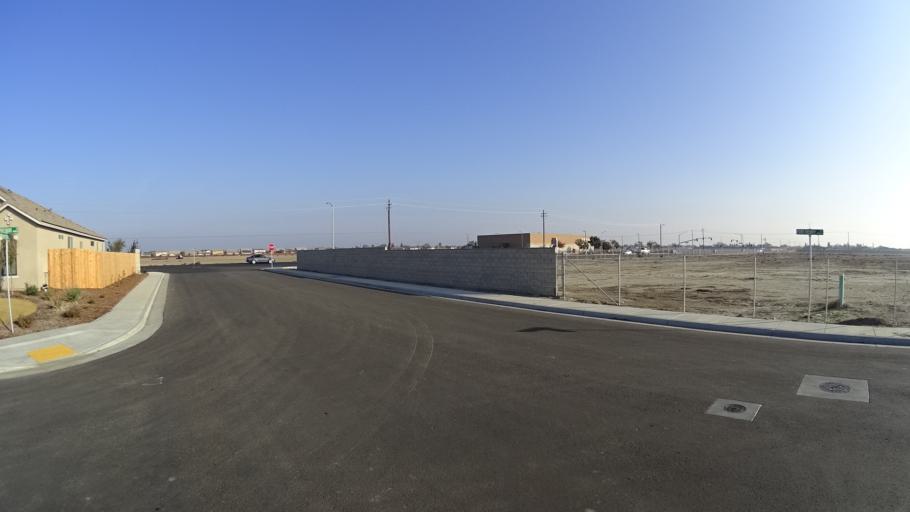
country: US
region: California
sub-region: Kern County
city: Greenacres
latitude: 35.2955
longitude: -119.1126
